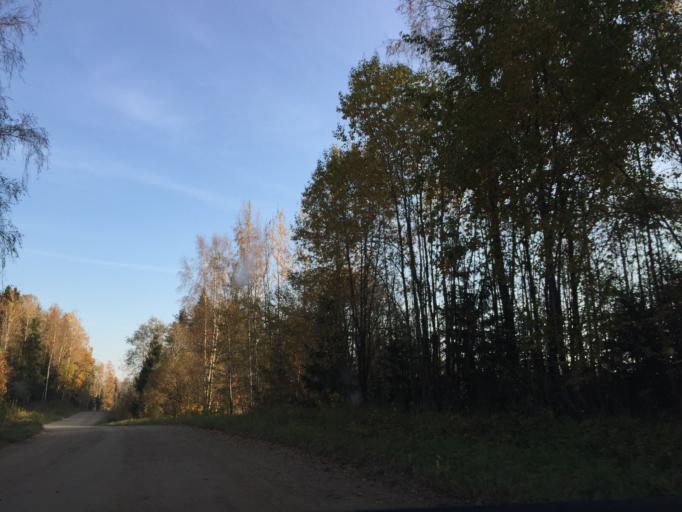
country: LV
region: Vainode
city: Vainode
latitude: 56.5958
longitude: 21.8320
